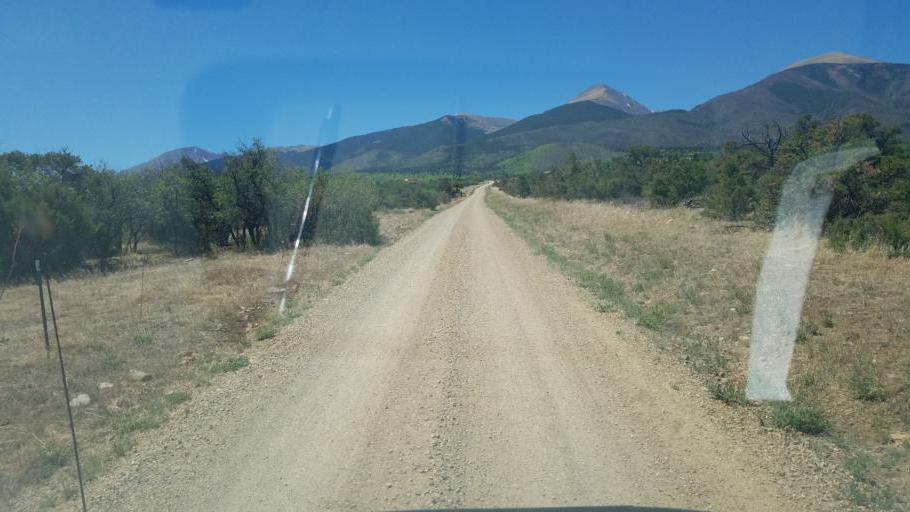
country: US
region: Colorado
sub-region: Custer County
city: Westcliffe
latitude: 38.3023
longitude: -105.6681
